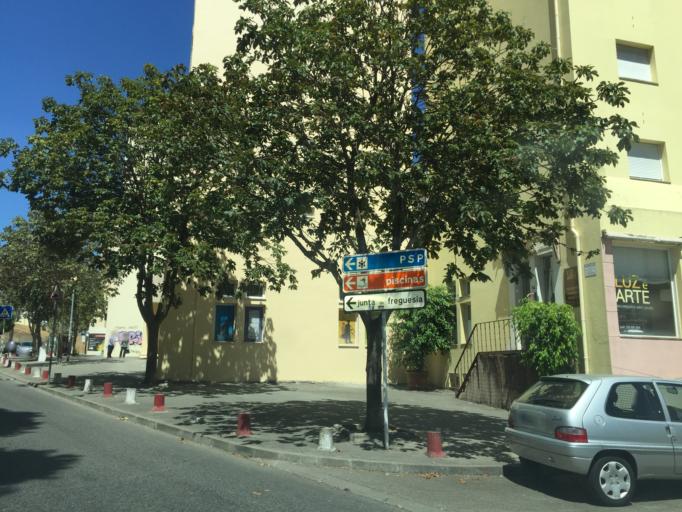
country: PT
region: Lisbon
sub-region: Odivelas
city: Povoa de Santo Adriao
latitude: 38.8099
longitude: -9.1617
